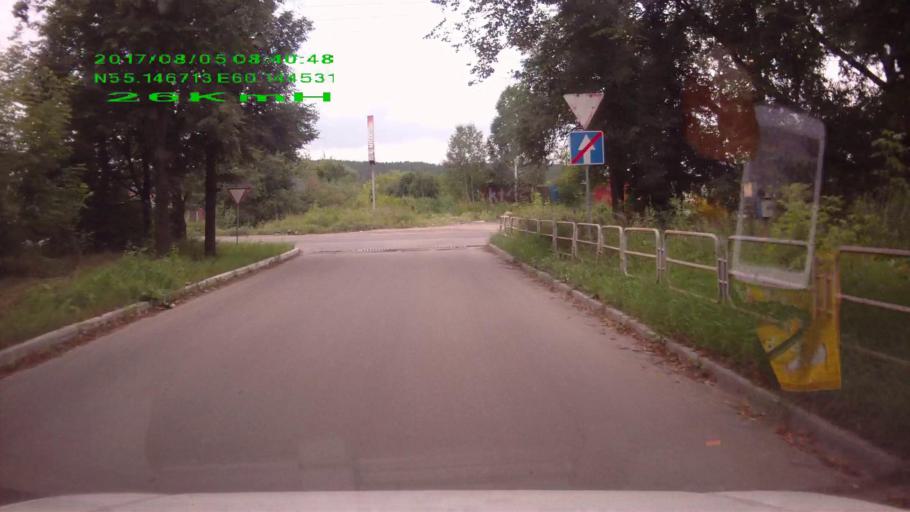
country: RU
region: Chelyabinsk
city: Turgoyak
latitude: 55.1467
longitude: 60.1443
